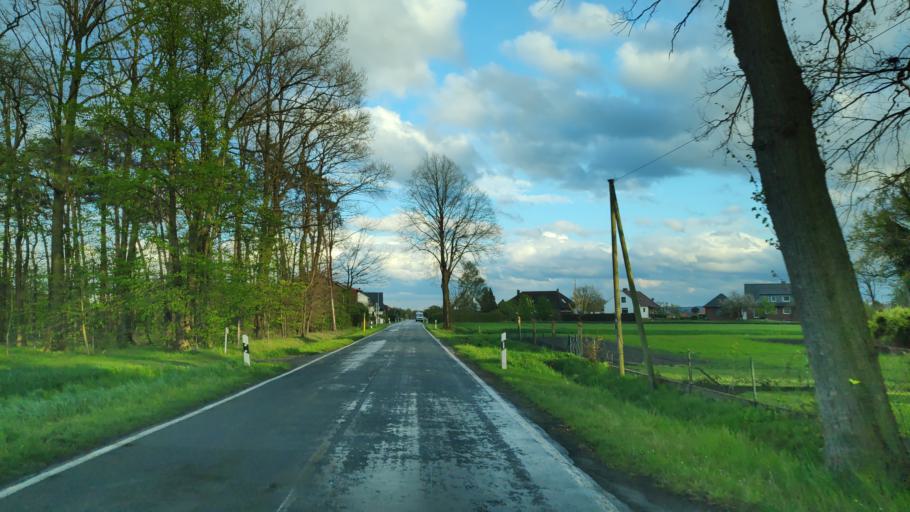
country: DE
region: North Rhine-Westphalia
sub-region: Regierungsbezirk Detmold
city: Hille
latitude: 52.3641
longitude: 8.8060
